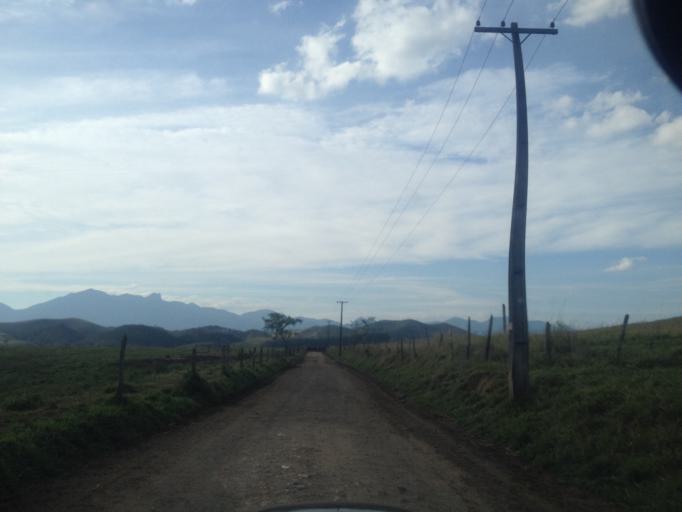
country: BR
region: Rio de Janeiro
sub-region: Resende
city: Resende
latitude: -22.4416
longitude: -44.3983
